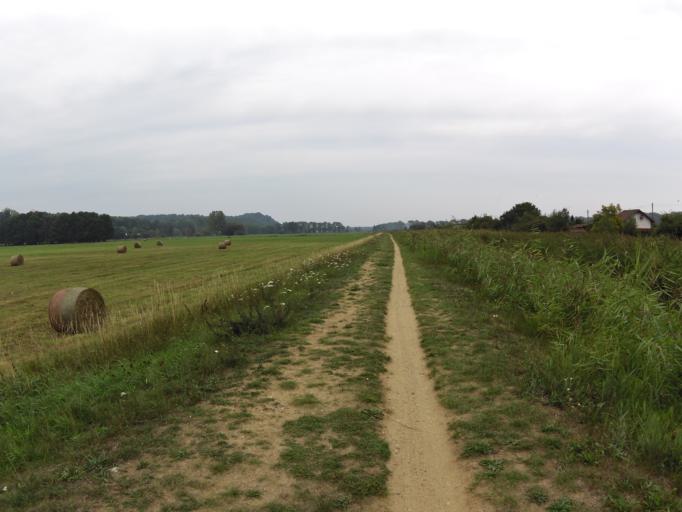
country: PL
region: West Pomeranian Voivodeship
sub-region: Swinoujscie
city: Swinoujscie
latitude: 53.8696
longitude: 14.2127
